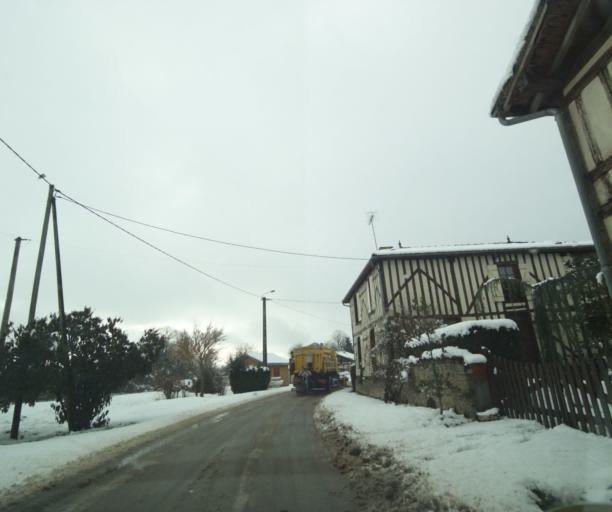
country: FR
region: Champagne-Ardenne
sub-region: Departement de la Haute-Marne
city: Montier-en-Der
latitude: 48.4940
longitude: 4.7012
